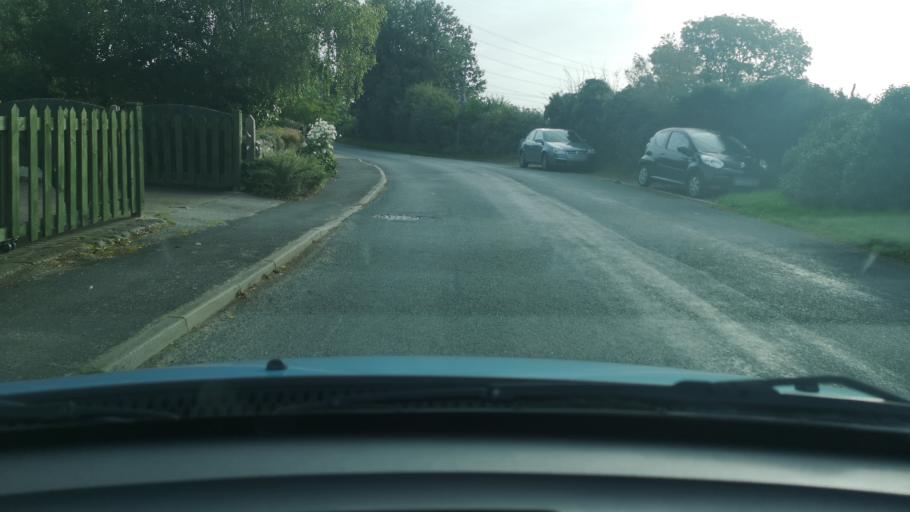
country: GB
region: England
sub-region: Doncaster
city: Askern
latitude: 53.6060
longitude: -1.1658
